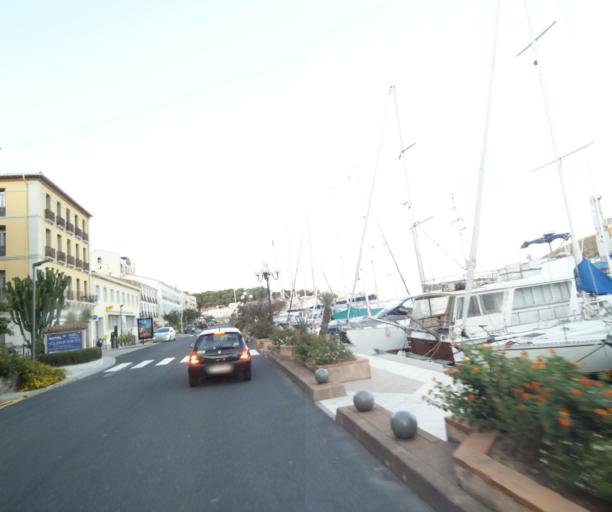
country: FR
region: Languedoc-Roussillon
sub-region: Departement des Pyrenees-Orientales
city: Portvendres
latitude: 42.5172
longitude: 3.1061
